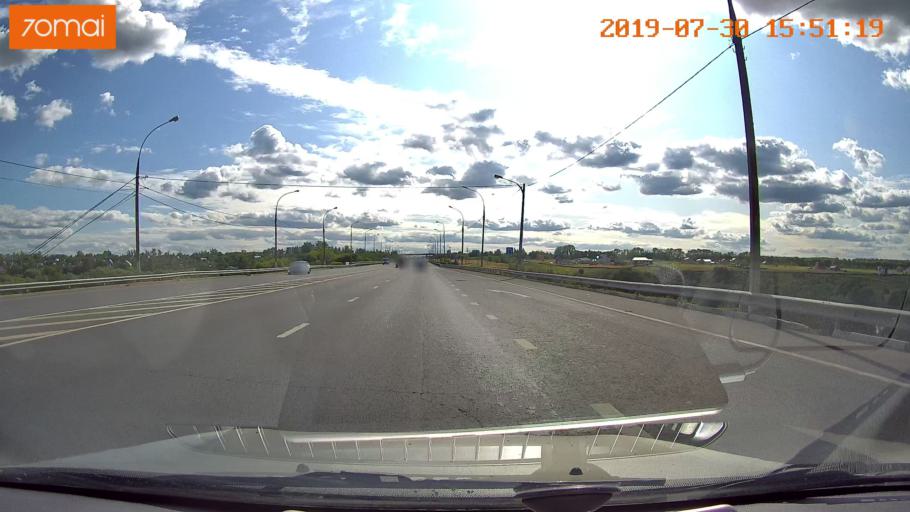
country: RU
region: Moskovskaya
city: Voskresensk
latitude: 55.3271
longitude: 38.6429
